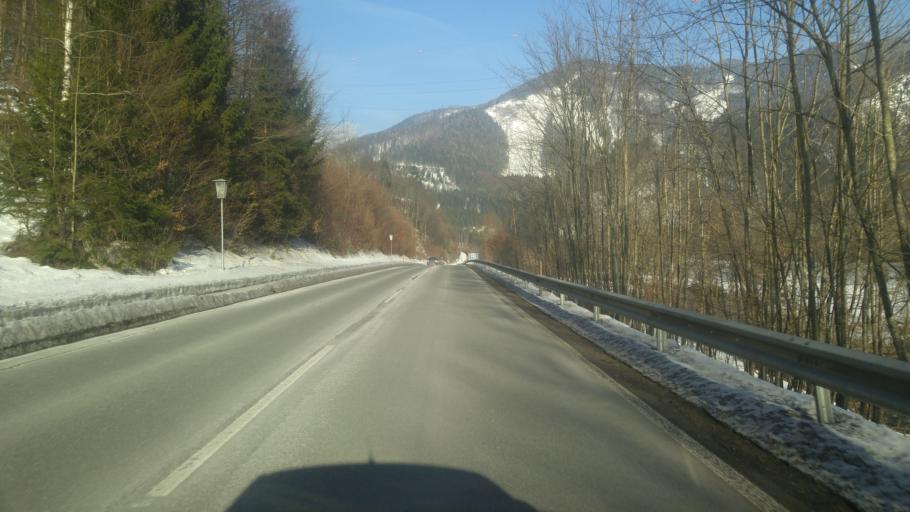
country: AT
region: Lower Austria
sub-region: Politischer Bezirk Lilienfeld
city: Lilienfeld
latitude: 47.9733
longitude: 15.5656
